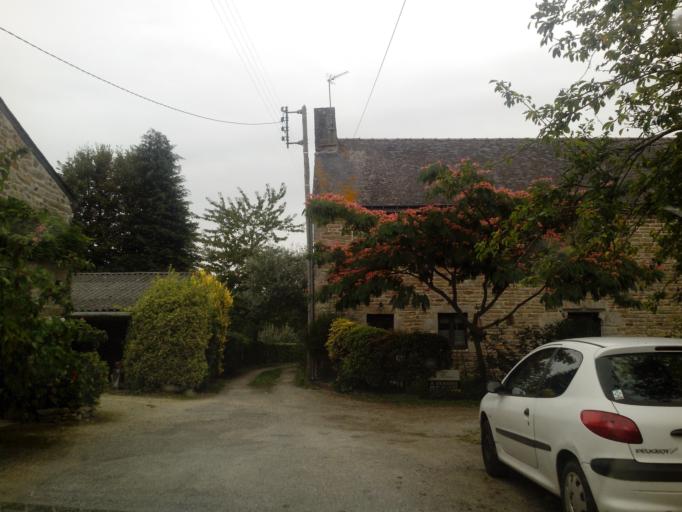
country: FR
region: Brittany
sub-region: Departement du Finistere
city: Querrien
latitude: 47.9448
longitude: -3.5028
